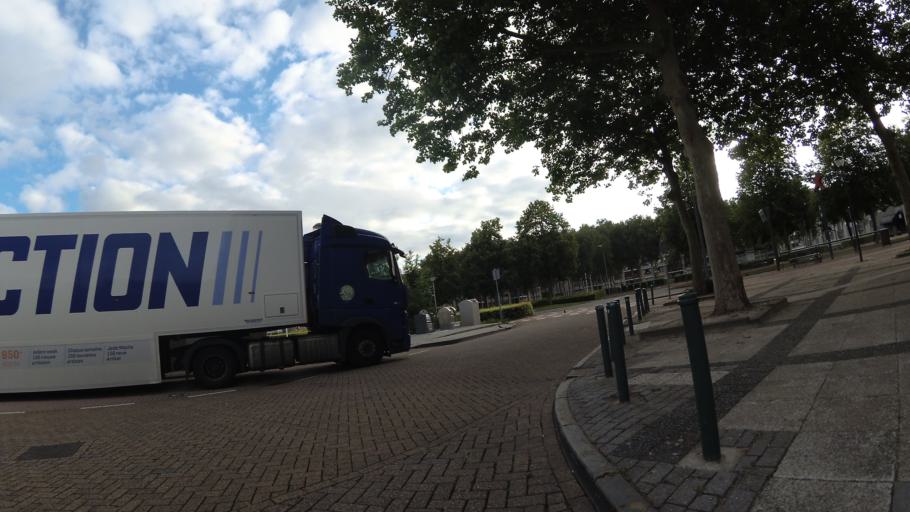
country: NL
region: North Brabant
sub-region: Gemeente Breda
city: Hoge Vucht
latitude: 51.6085
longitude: 4.7907
